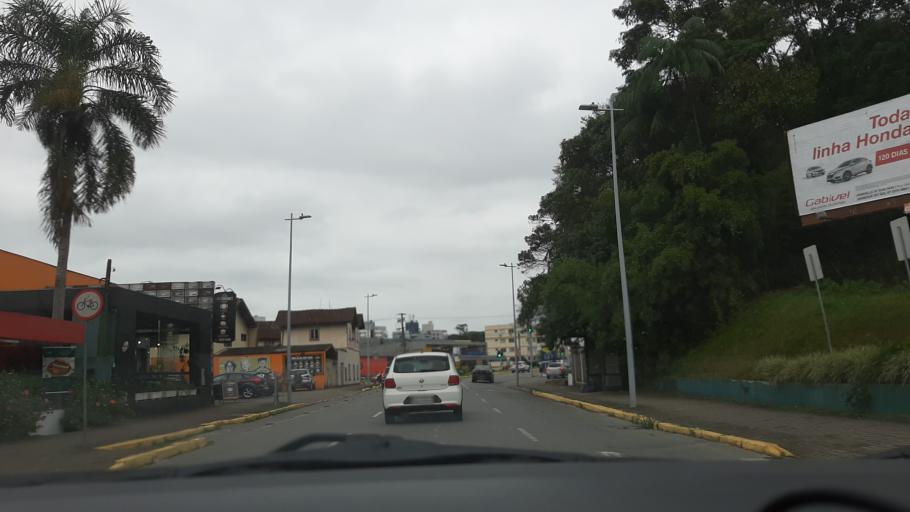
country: BR
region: Santa Catarina
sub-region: Joinville
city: Joinville
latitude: -26.3096
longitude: -48.8548
